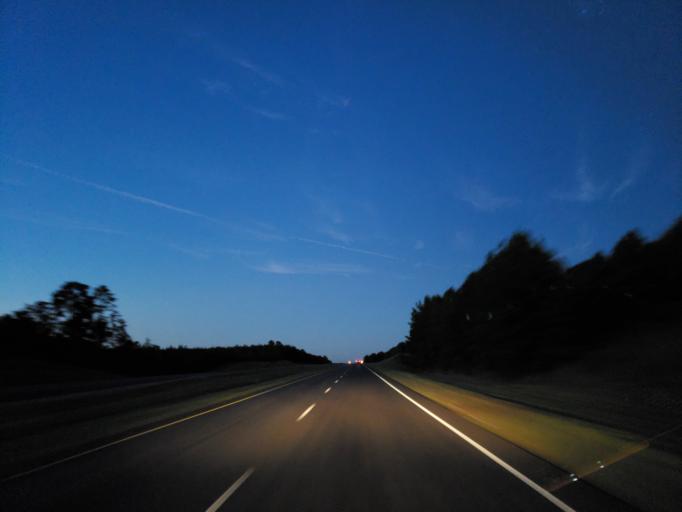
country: US
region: Mississippi
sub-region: Clarke County
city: Quitman
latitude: 32.0178
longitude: -88.6860
